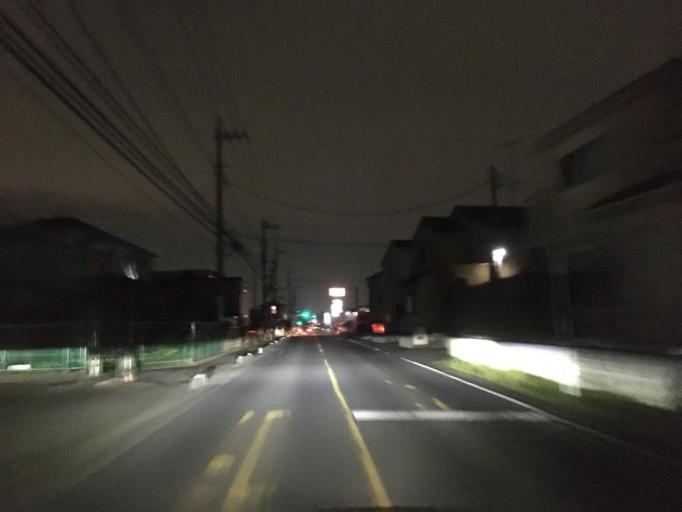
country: JP
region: Saitama
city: Tokorozawa
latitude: 35.8215
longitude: 139.4402
